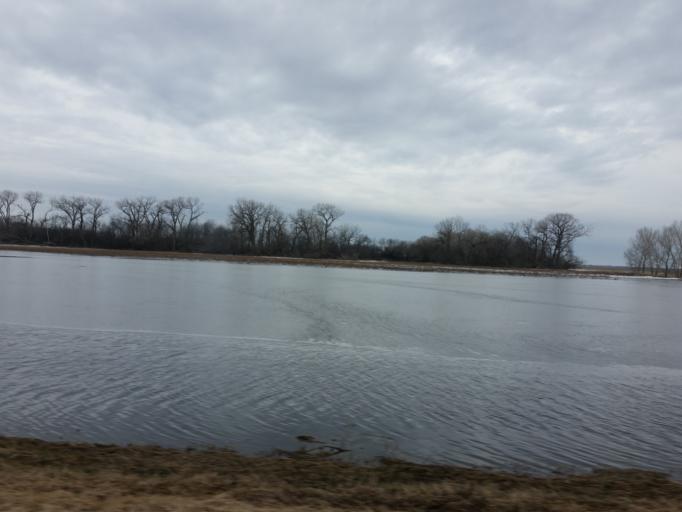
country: US
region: North Dakota
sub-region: Walsh County
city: Grafton
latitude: 48.4044
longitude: -97.4703
